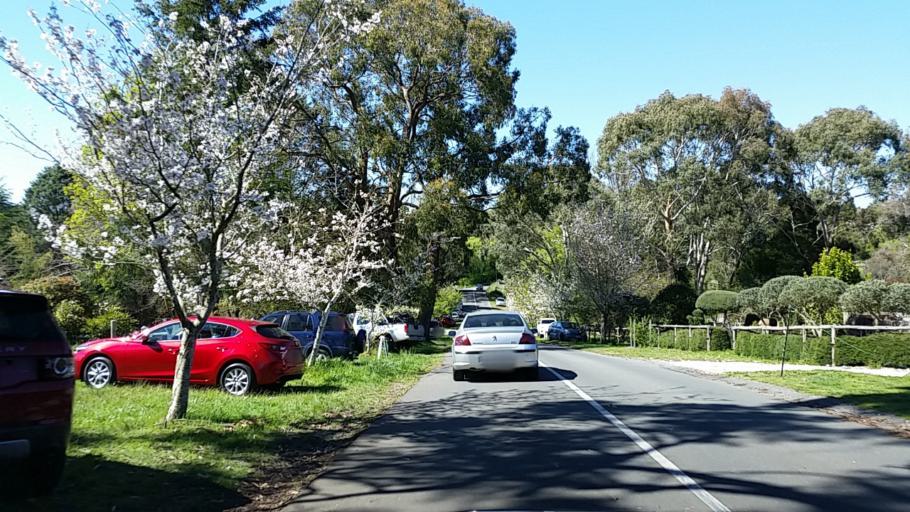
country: AU
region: South Australia
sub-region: Adelaide Hills
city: Crafers
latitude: -34.9851
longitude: 138.7215
